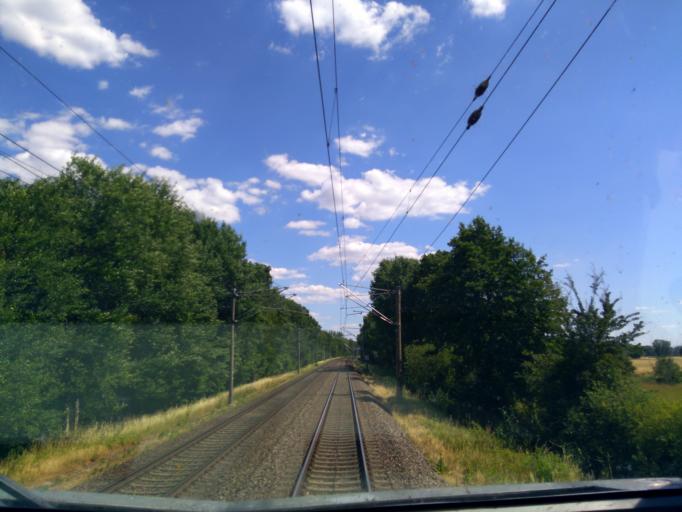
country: DE
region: Brandenburg
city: Bad Wilsnack
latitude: 52.9688
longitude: 11.9256
